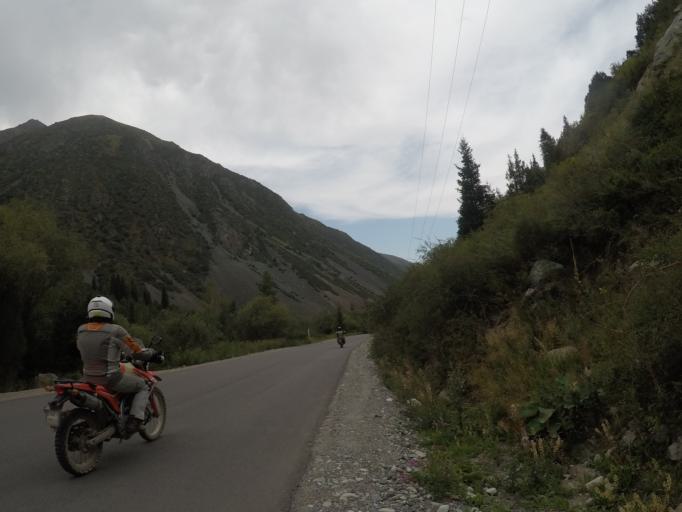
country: KG
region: Chuy
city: Bishkek
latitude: 42.5763
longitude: 74.4821
